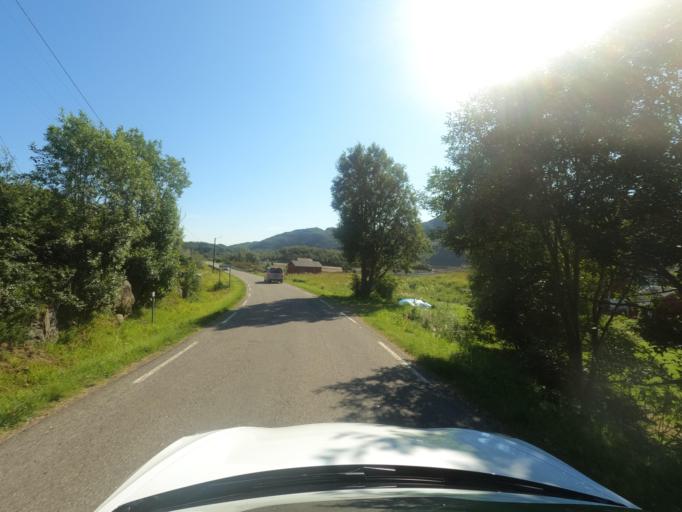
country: NO
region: Nordland
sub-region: Hadsel
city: Stokmarknes
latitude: 68.3051
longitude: 14.9989
